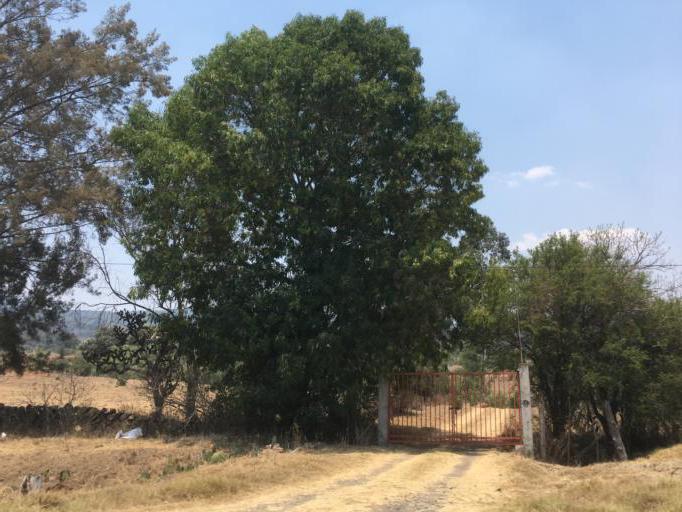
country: MX
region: Michoacan
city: Quiroga
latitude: 19.6495
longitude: -101.4926
